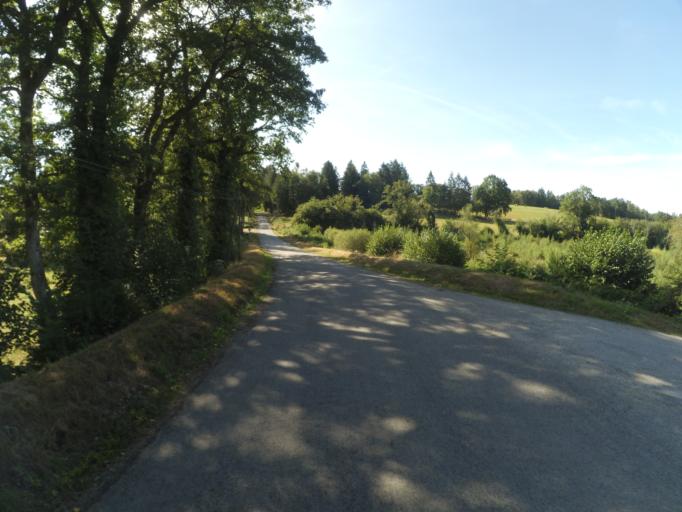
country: FR
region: Limousin
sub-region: Departement de la Correze
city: Bugeat
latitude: 45.7066
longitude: 1.8690
